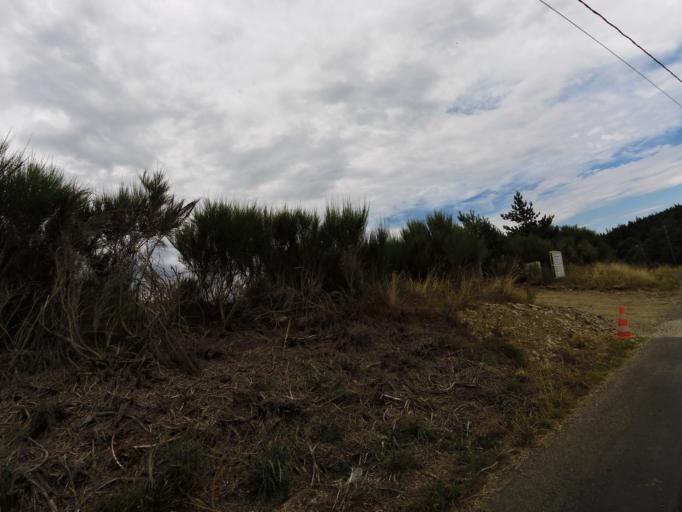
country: FR
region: Languedoc-Roussillon
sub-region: Departement du Gard
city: Valleraugue
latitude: 44.0906
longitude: 3.5517
